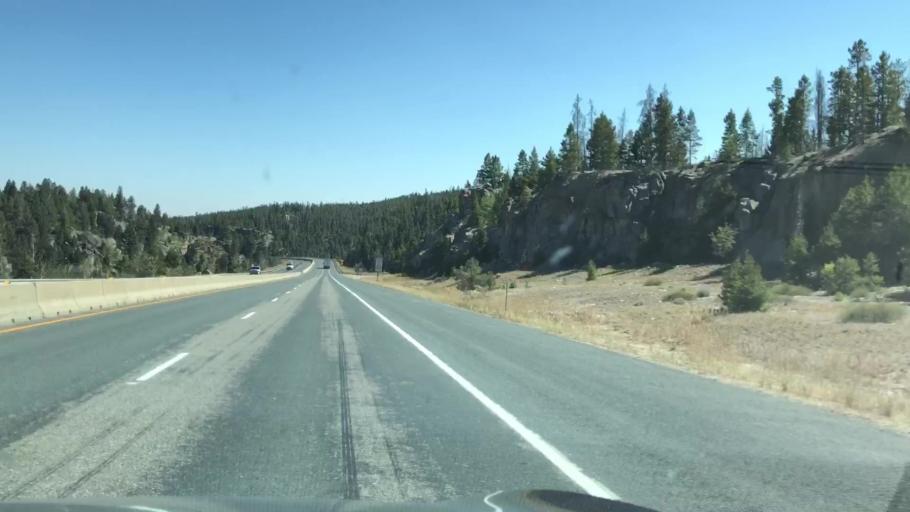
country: US
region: Montana
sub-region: Silver Bow County
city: Butte
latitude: 45.9121
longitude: -112.3581
